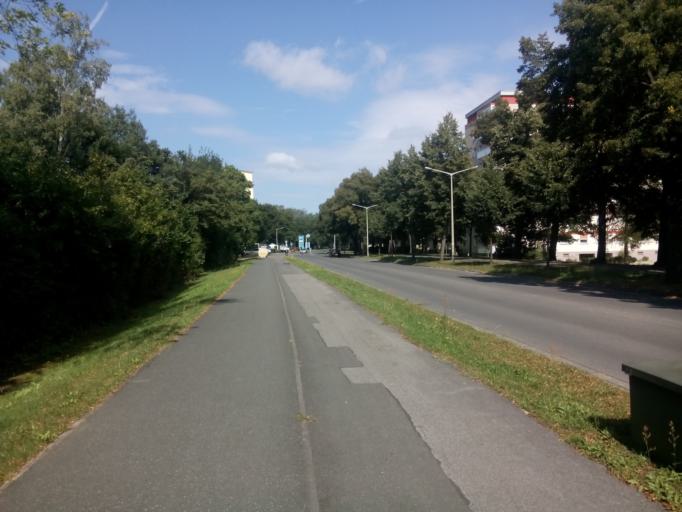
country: DE
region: Bavaria
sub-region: Upper Franconia
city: Bamberg
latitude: 49.8854
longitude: 10.9096
